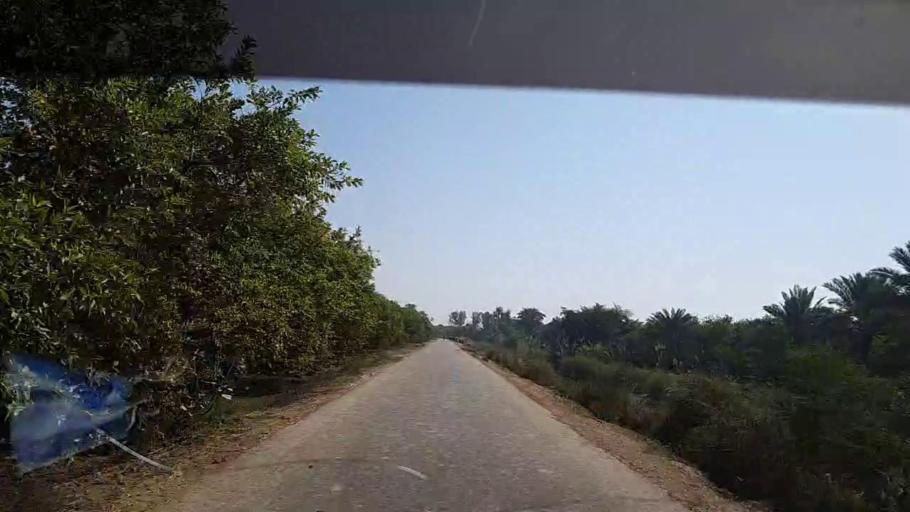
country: PK
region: Sindh
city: Larkana
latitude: 27.6029
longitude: 68.2650
